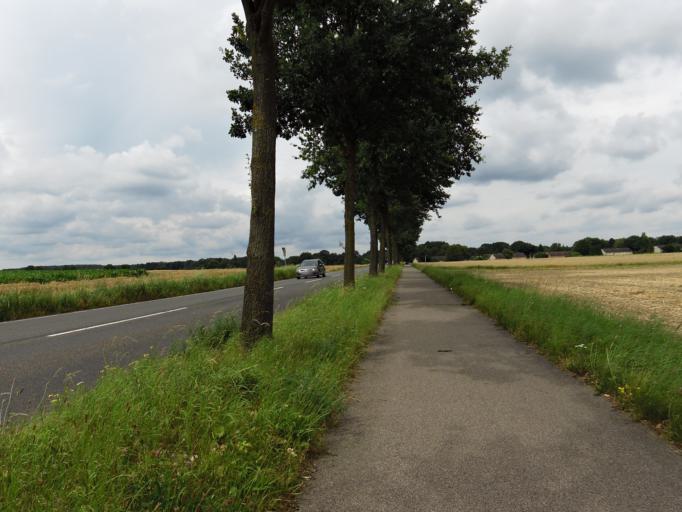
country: DE
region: North Rhine-Westphalia
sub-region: Regierungsbezirk Koln
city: Ubach-Palenberg
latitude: 50.9508
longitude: 6.0701
